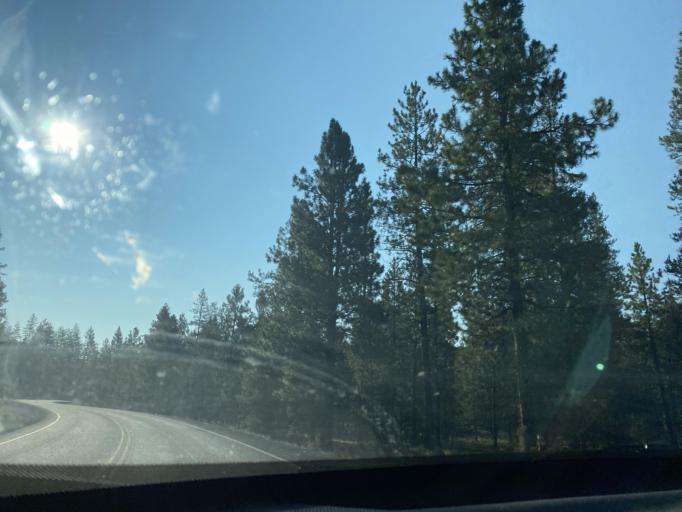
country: US
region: Oregon
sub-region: Deschutes County
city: La Pine
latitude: 43.7079
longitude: -121.4053
